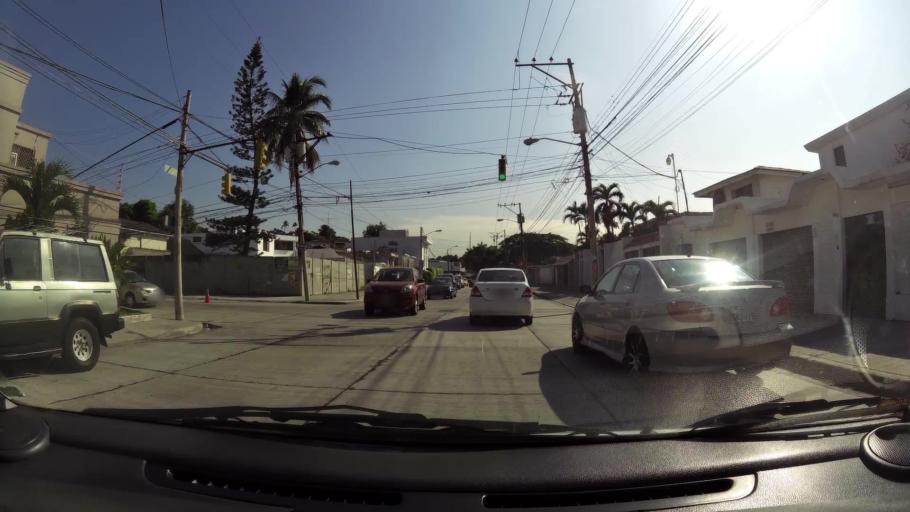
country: EC
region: Guayas
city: Guayaquil
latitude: -2.1693
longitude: -79.9025
